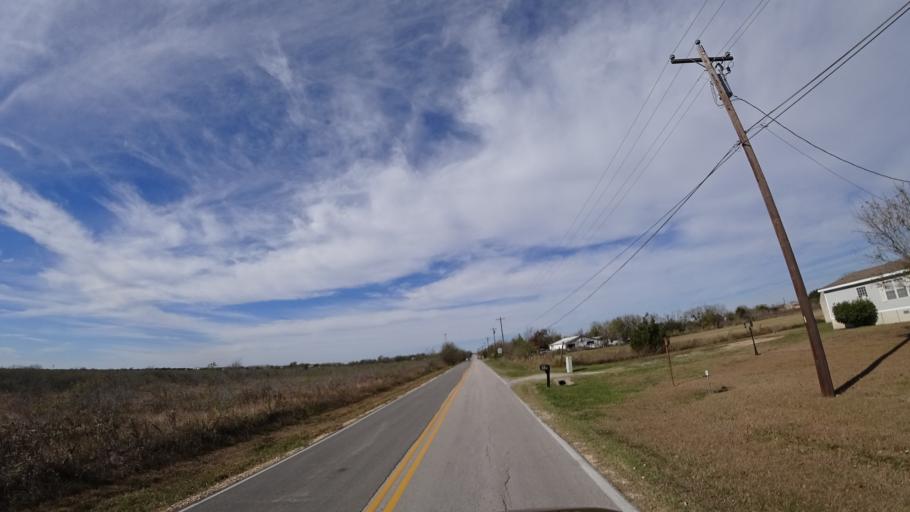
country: US
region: Texas
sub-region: Travis County
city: Onion Creek
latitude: 30.1118
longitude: -97.6960
